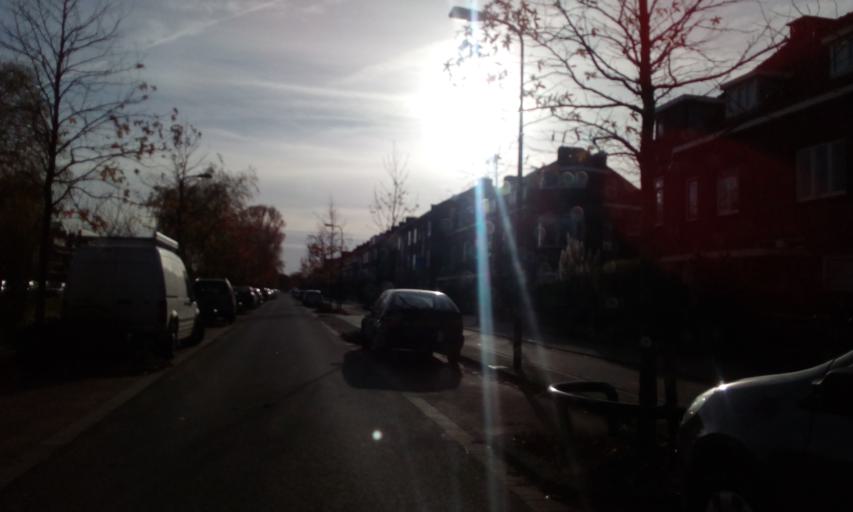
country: NL
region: South Holland
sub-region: Gemeente Rijswijk
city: Rijswijk
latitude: 52.0543
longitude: 4.3331
